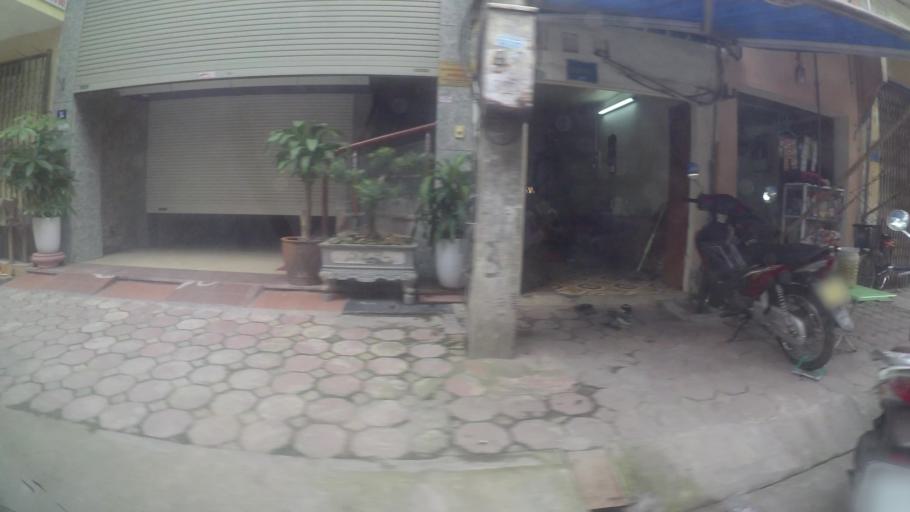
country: VN
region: Ha Noi
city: Ha Dong
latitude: 20.9714
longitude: 105.7720
